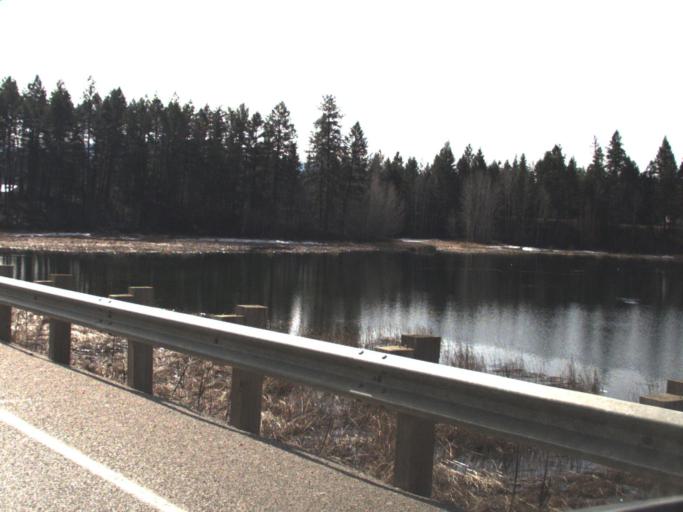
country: US
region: Washington
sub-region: Stevens County
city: Colville
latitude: 48.5202
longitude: -117.8118
